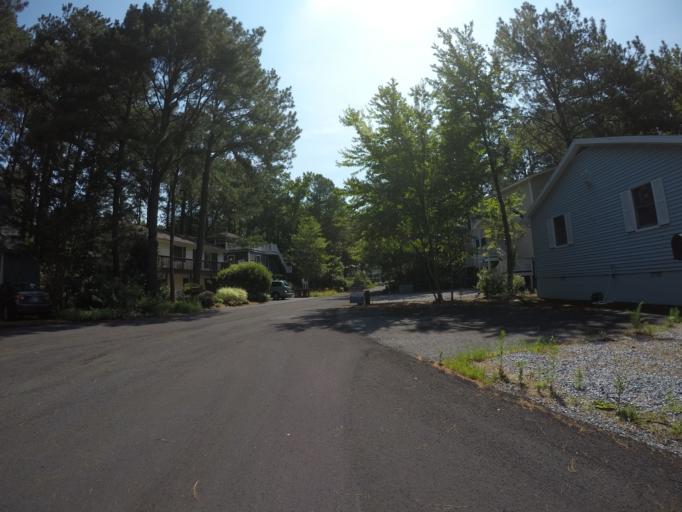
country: US
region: Delaware
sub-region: Sussex County
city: Bethany Beach
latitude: 38.5203
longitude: -75.0595
